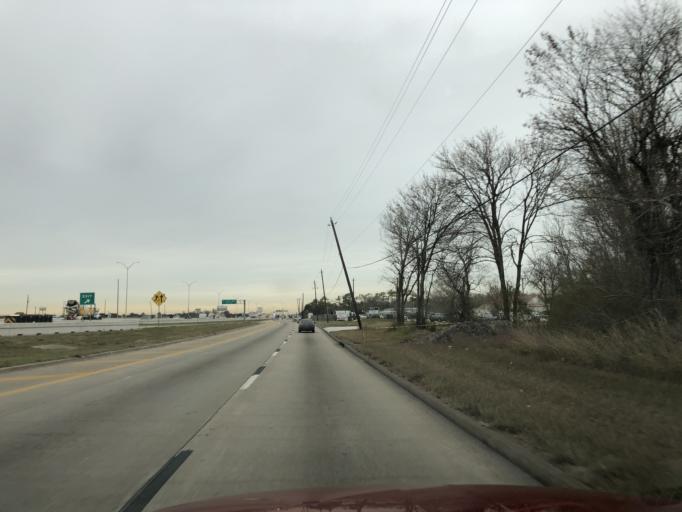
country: US
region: Texas
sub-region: Fort Bend County
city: Missouri City
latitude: 29.6301
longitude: -95.5217
